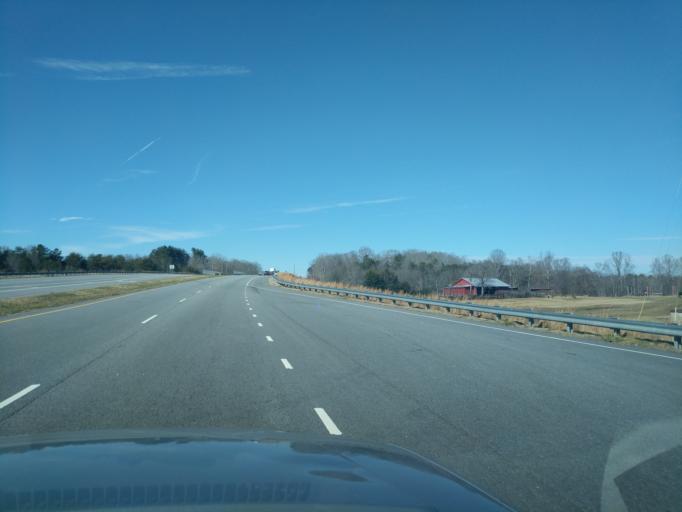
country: US
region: North Carolina
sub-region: Rutherford County
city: Forest City
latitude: 35.2473
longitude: -81.8696
